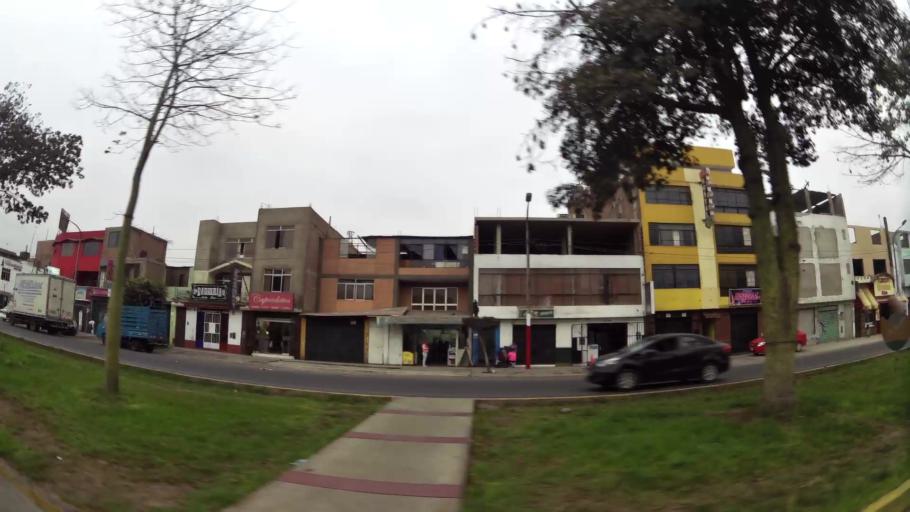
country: PE
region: Lima
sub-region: Lima
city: Independencia
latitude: -12.0072
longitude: -77.0092
